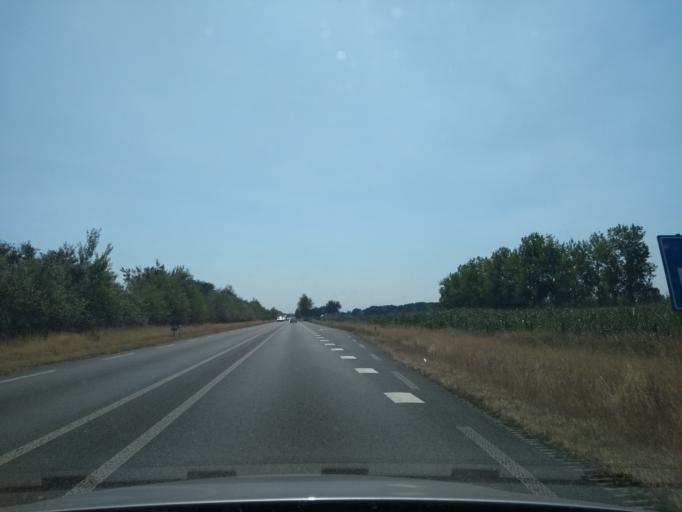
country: NL
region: Overijssel
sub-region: Gemeente Wierden
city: Wierden
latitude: 52.3070
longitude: 6.5516
